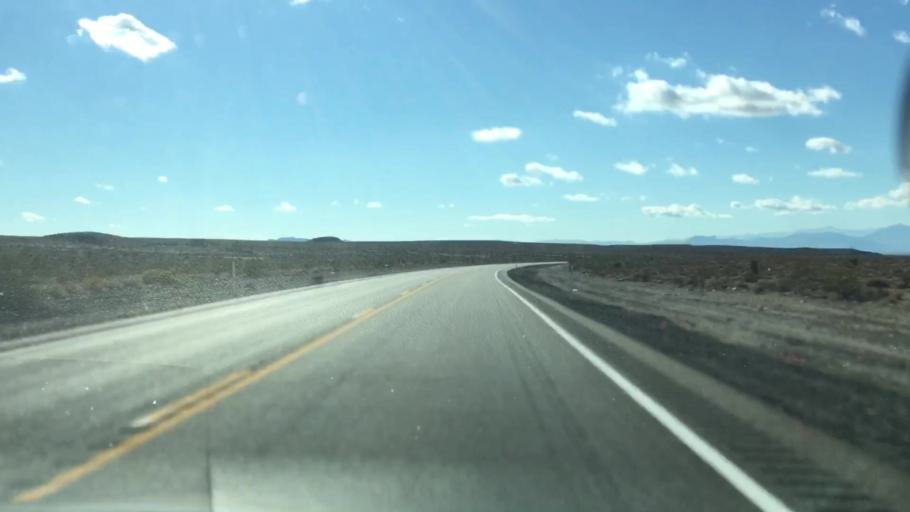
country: US
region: Nevada
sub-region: Nye County
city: Pahrump
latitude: 36.5655
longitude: -116.0837
